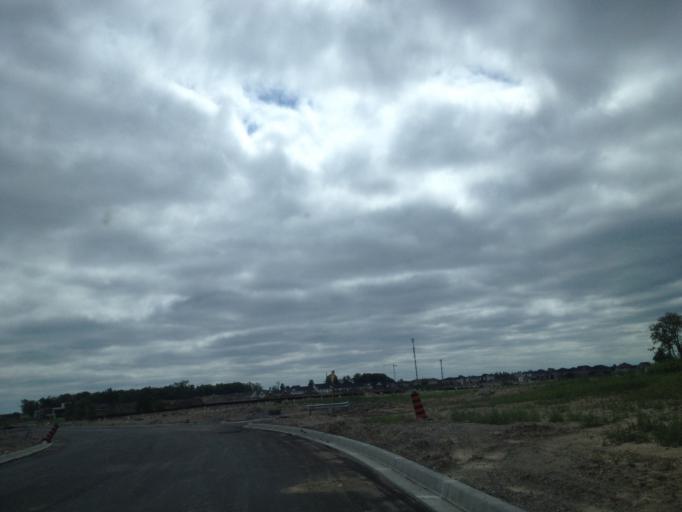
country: CA
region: Ontario
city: London
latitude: 43.0235
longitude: -81.3322
